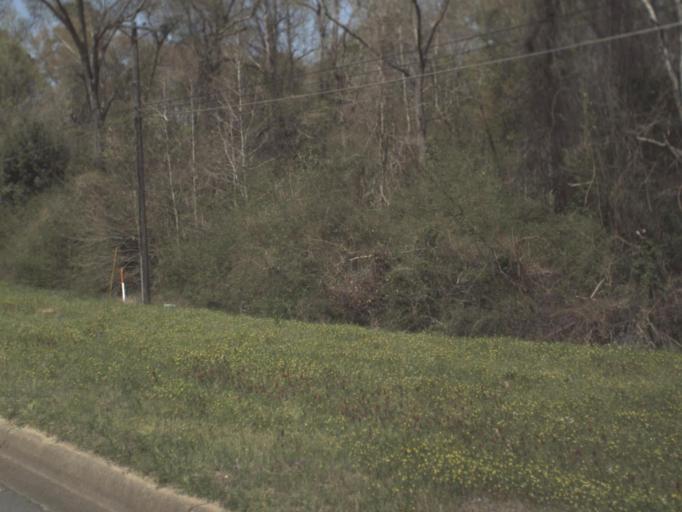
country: US
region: Florida
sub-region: Gadsden County
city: Quincy
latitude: 30.5793
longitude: -84.5591
